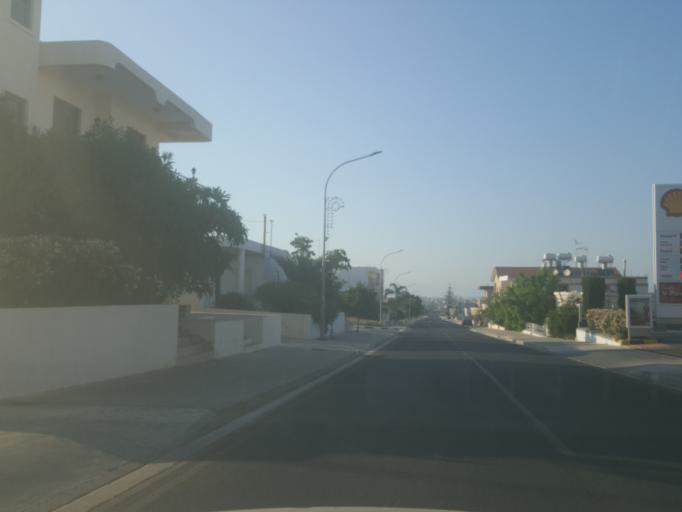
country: CY
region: Ammochostos
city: Deryneia
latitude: 35.0678
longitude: 33.9608
